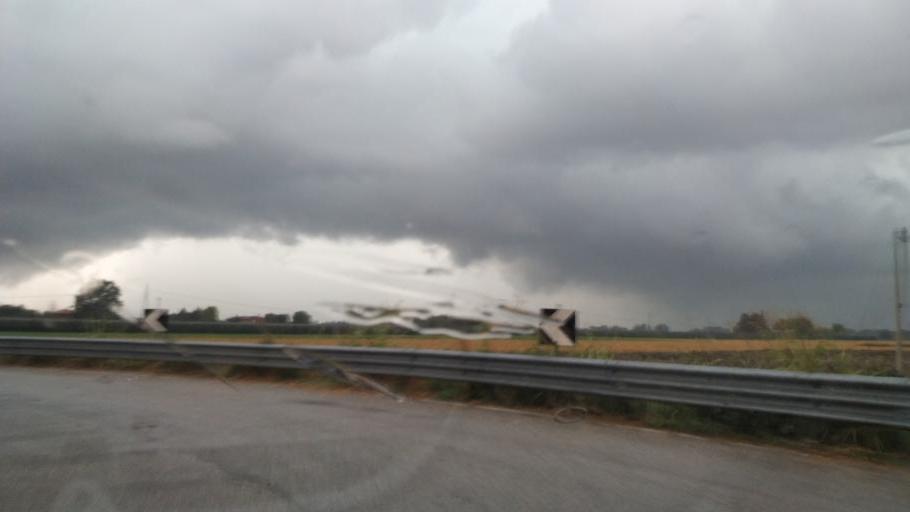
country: IT
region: Emilia-Romagna
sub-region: Provincia di Ferrara
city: Pontegradella
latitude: 44.8576
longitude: 11.6778
